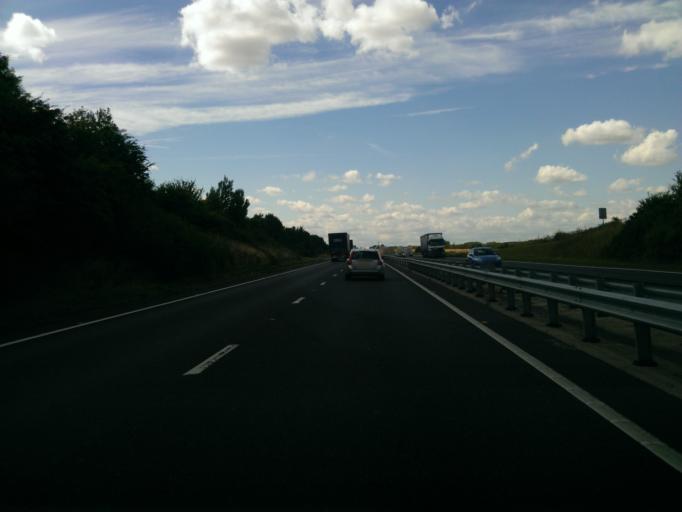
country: GB
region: England
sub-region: Bedford
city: Pertenhall
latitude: 52.3455
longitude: -0.3484
